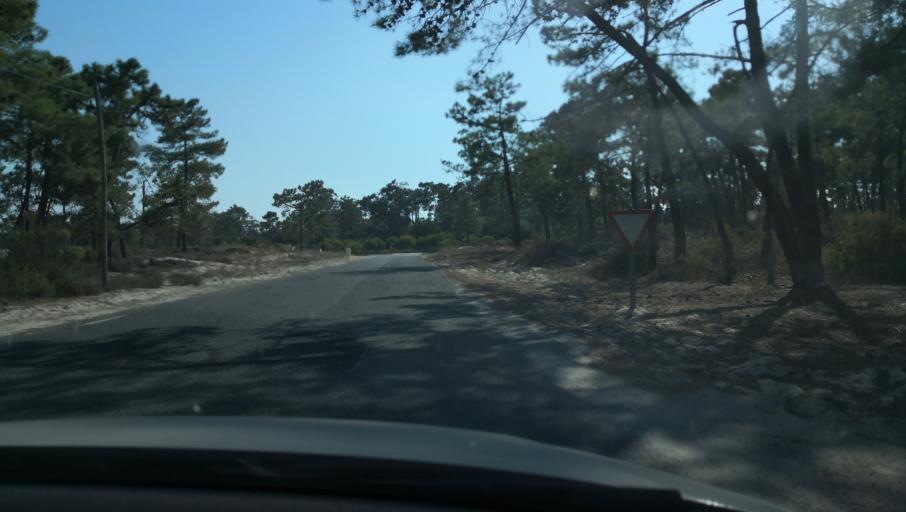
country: PT
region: Setubal
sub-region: Setubal
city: Setubal
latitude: 38.4663
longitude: -8.8699
